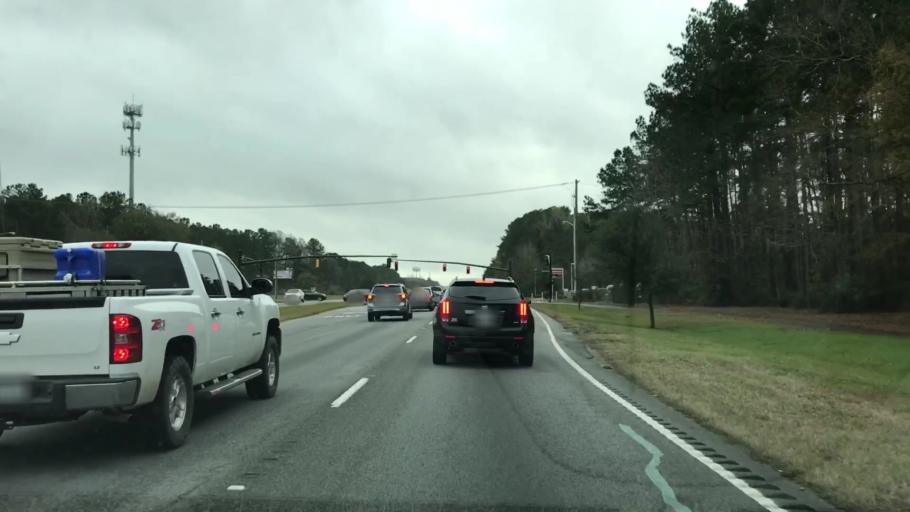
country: US
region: South Carolina
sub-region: Berkeley County
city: Goose Creek
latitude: 33.0194
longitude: -80.0361
